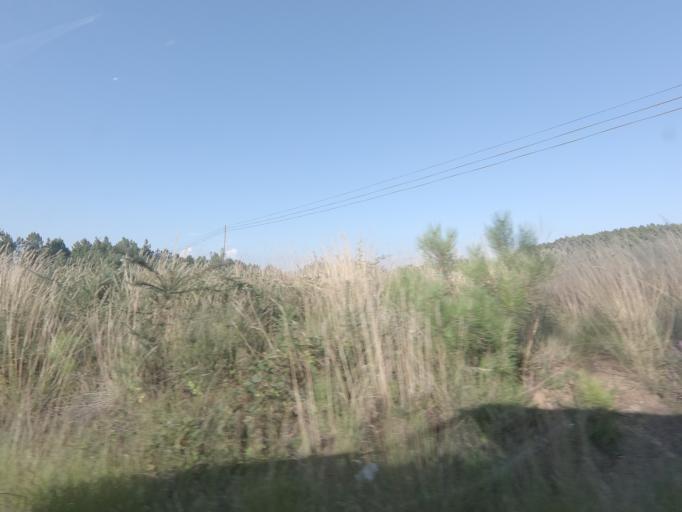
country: PT
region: Vila Real
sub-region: Sabrosa
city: Vilela
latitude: 41.2439
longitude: -7.6040
